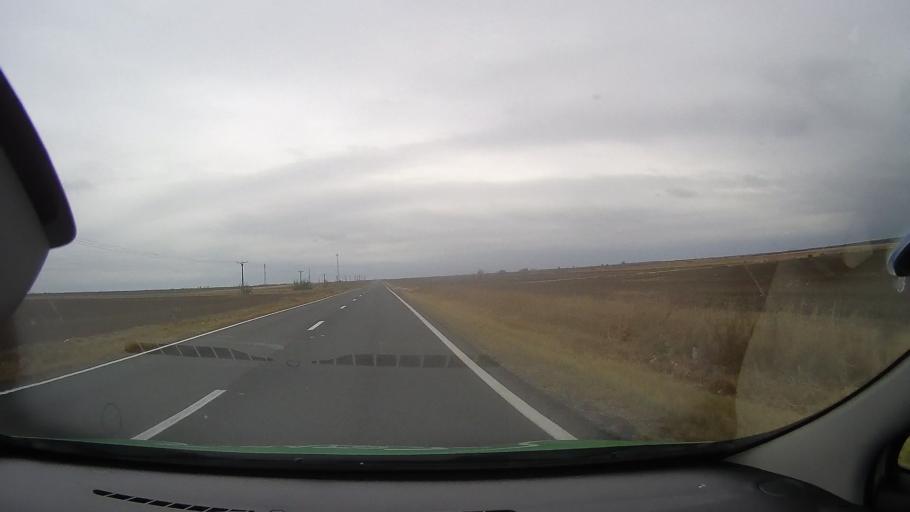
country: RO
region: Constanta
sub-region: Comuna Nicolae Balcescu
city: Nicolae Balcescu
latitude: 44.3769
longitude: 28.4187
